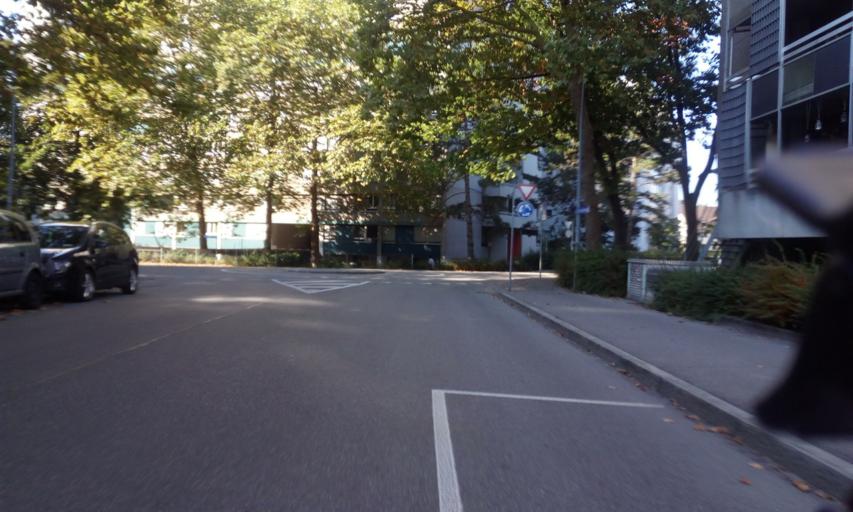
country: CH
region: Bern
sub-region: Bern-Mittelland District
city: Koniz
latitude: 46.9453
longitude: 7.3888
